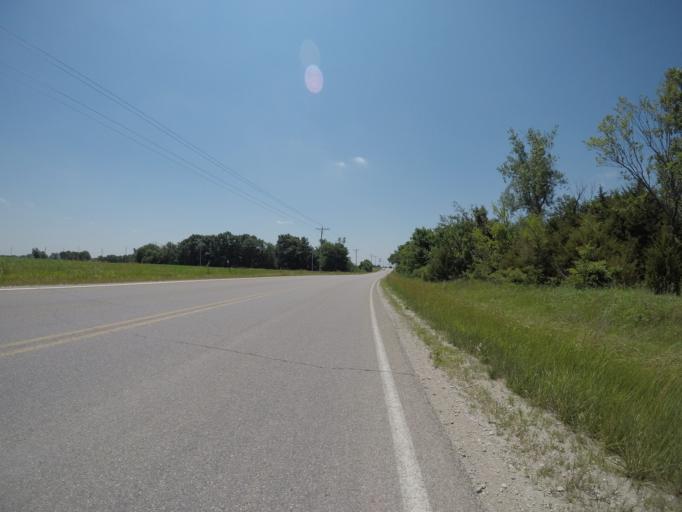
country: US
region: Kansas
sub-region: Pottawatomie County
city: Wamego
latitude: 39.2306
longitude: -96.4408
